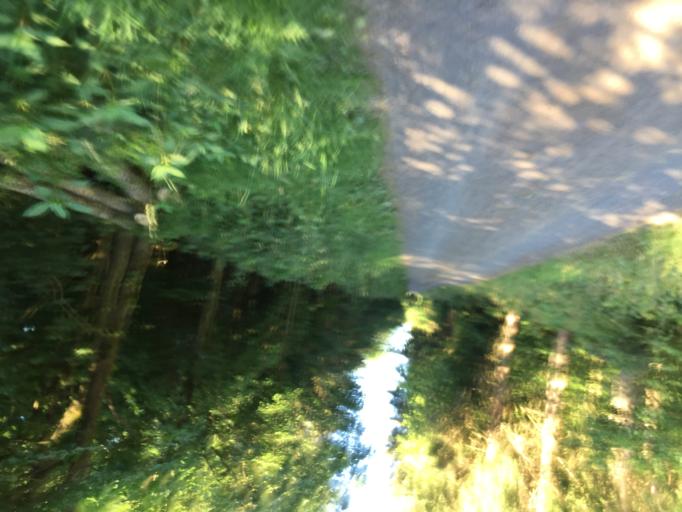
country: DE
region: Rheinland-Pfalz
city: Berod bei Wallmerod
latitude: 50.4936
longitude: 7.9291
